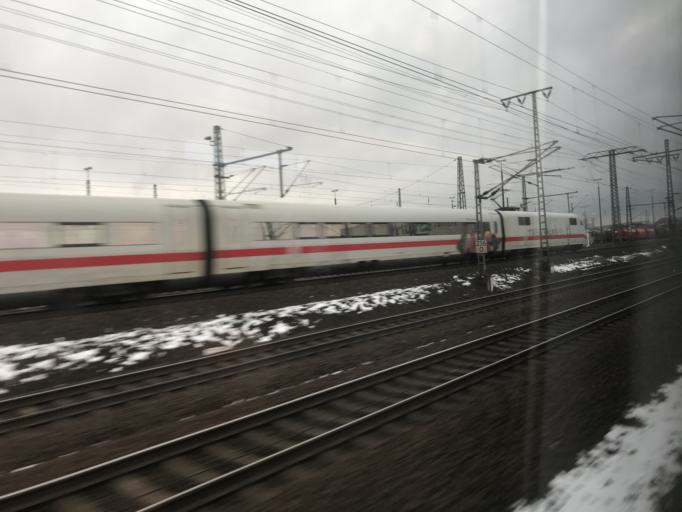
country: DE
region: Hesse
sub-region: Regierungsbezirk Kassel
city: Fulda
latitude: 50.5388
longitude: 9.6901
